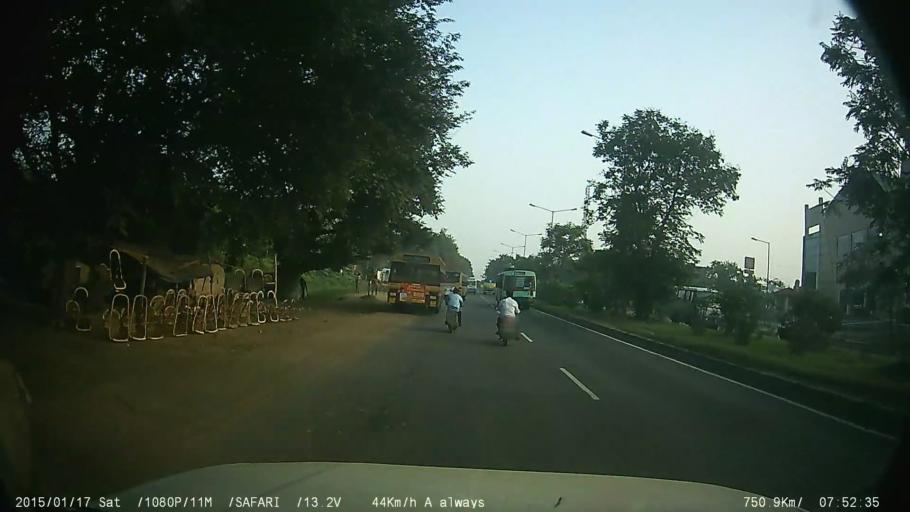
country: IN
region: Tamil Nadu
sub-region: Kancheepuram
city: Vandalur
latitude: 12.8761
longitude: 80.0788
